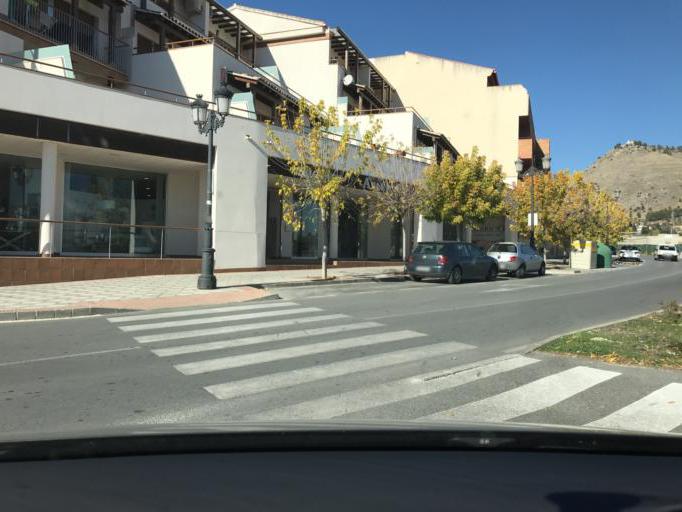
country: ES
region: Andalusia
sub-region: Provincia de Granada
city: Atarfe
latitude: 37.2265
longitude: -3.6785
